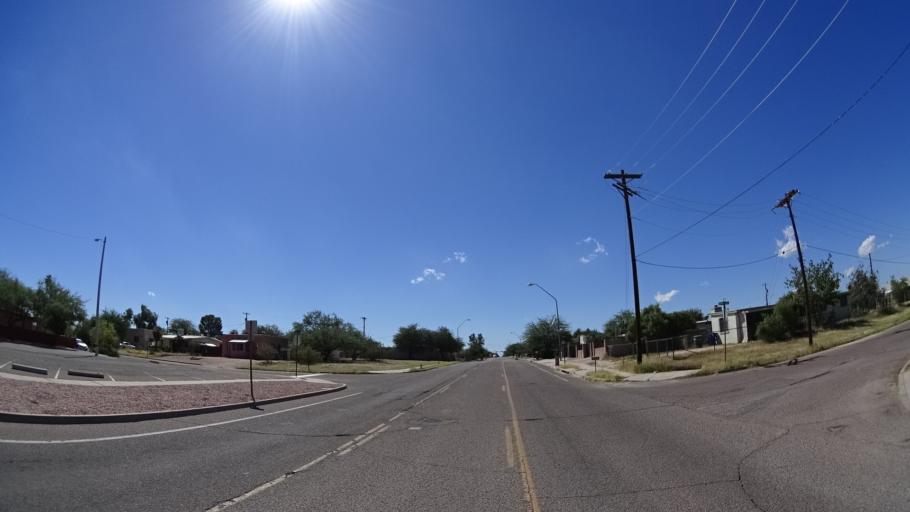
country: US
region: Arizona
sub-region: Pima County
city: South Tucson
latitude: 32.2429
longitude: -110.9687
